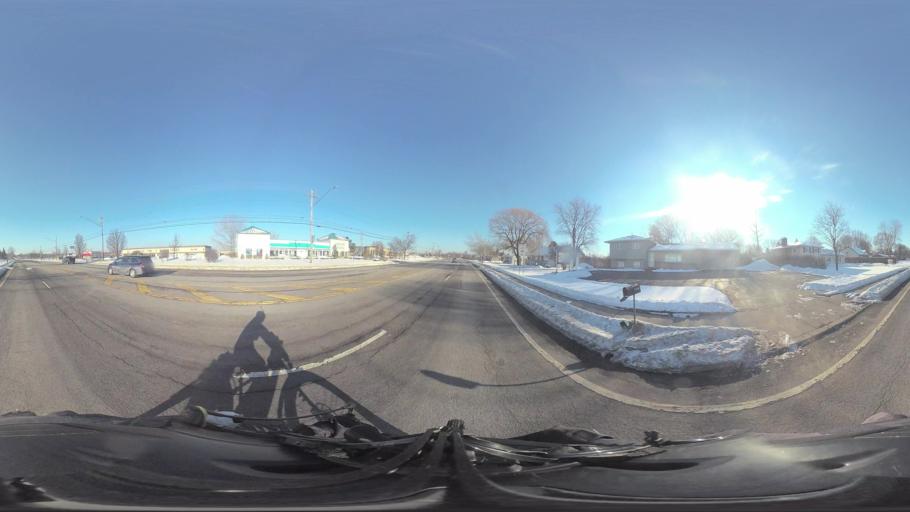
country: US
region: New York
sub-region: Monroe County
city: Rochester
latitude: 43.0663
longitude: -77.6087
